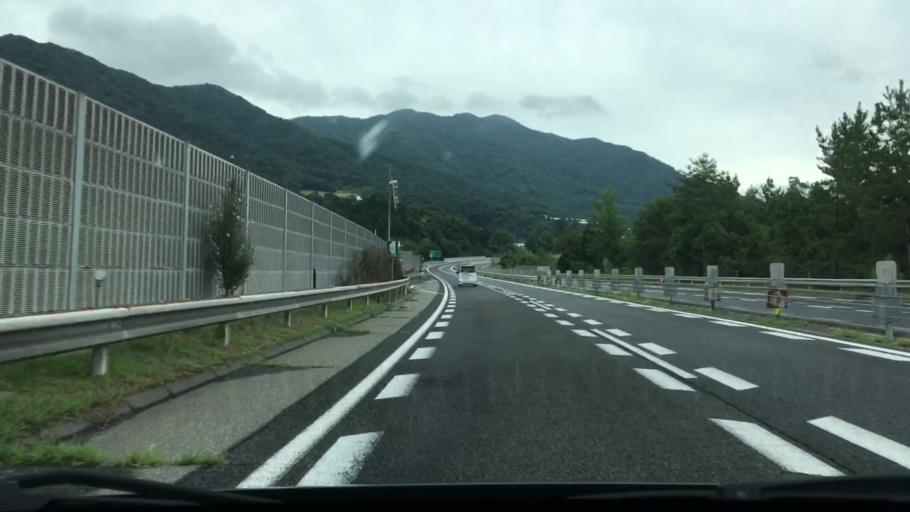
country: JP
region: Hiroshima
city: Hiroshima-shi
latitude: 34.6479
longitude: 132.5168
